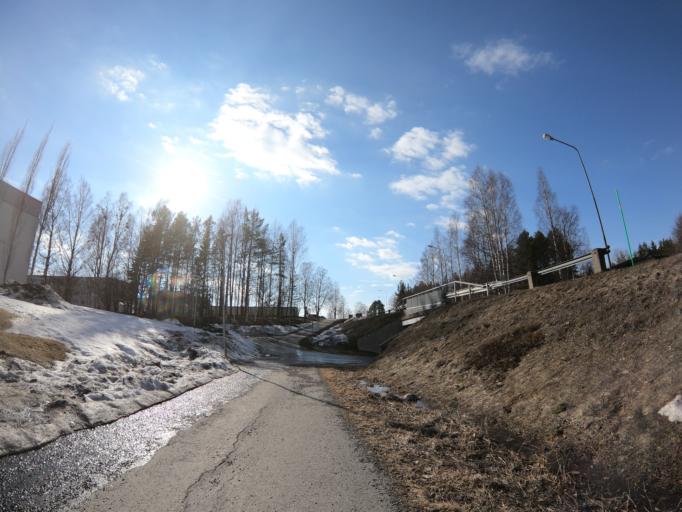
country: SE
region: Vaesterbotten
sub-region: Umea Kommun
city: Ersmark
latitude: 63.8378
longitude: 20.3292
